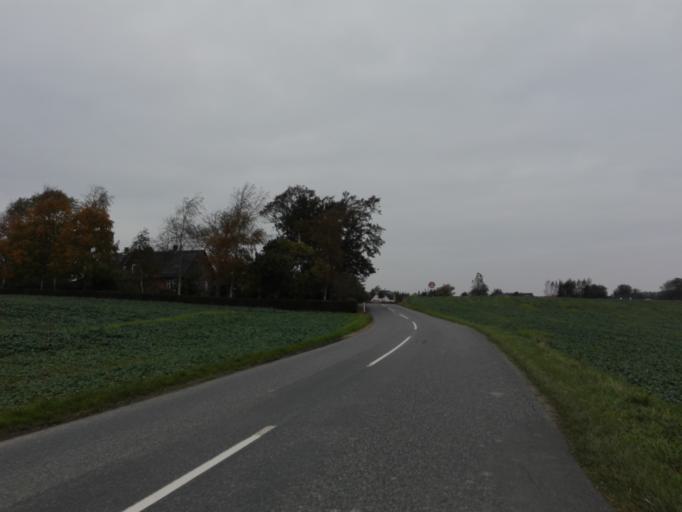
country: DK
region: Central Jutland
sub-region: Arhus Kommune
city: Beder
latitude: 56.0434
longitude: 10.2395
